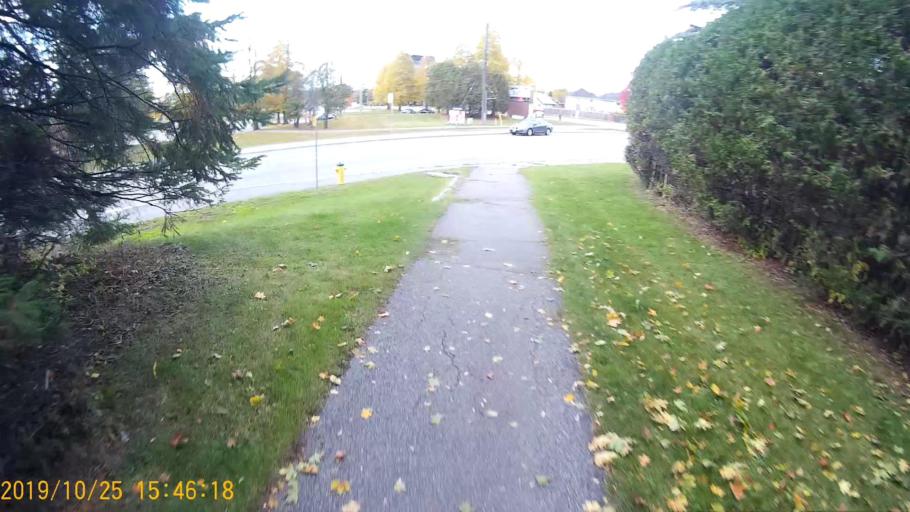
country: CA
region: Ontario
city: Bells Corners
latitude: 45.3018
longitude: -75.8836
